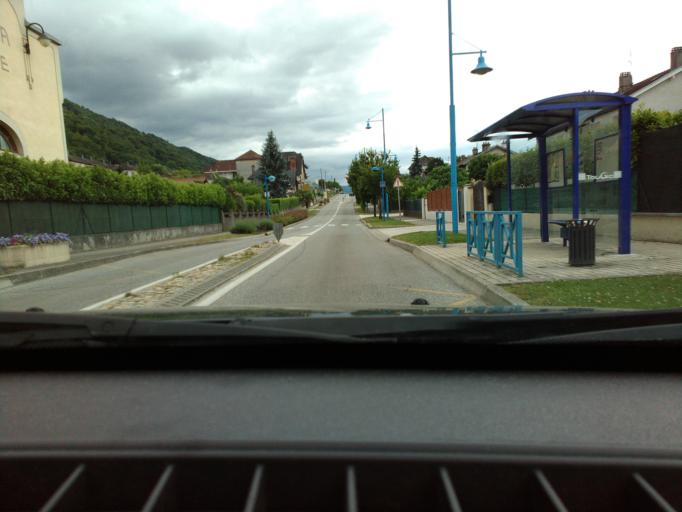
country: FR
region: Rhone-Alpes
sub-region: Departement de l'Isere
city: Froges
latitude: 45.2622
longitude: 5.9124
